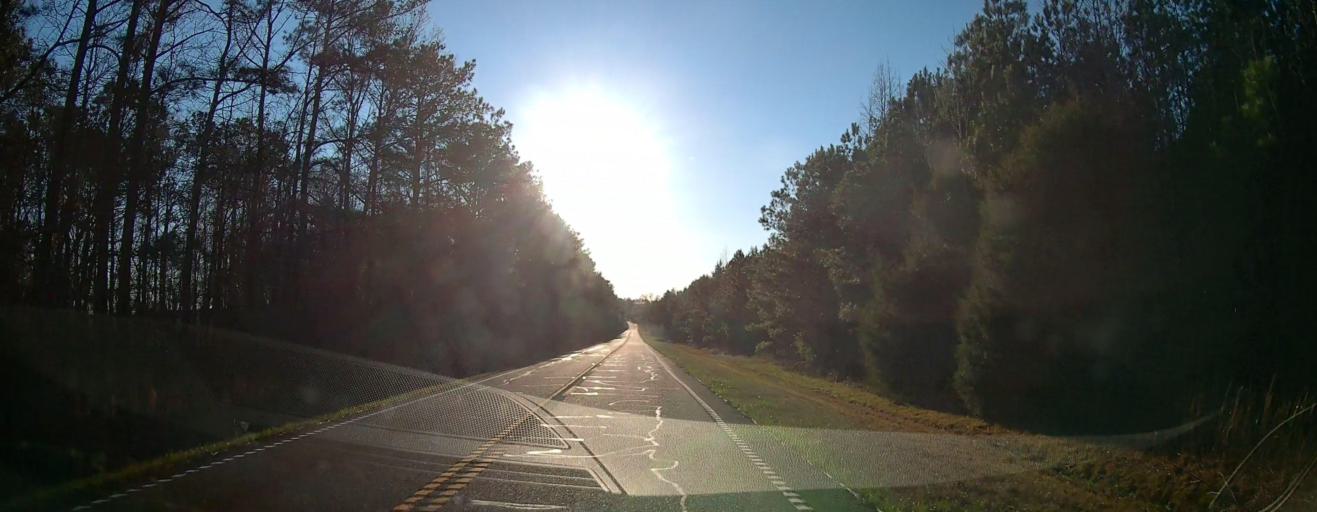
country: US
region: Georgia
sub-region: Talbot County
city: Talbotton
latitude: 32.6481
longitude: -84.6869
